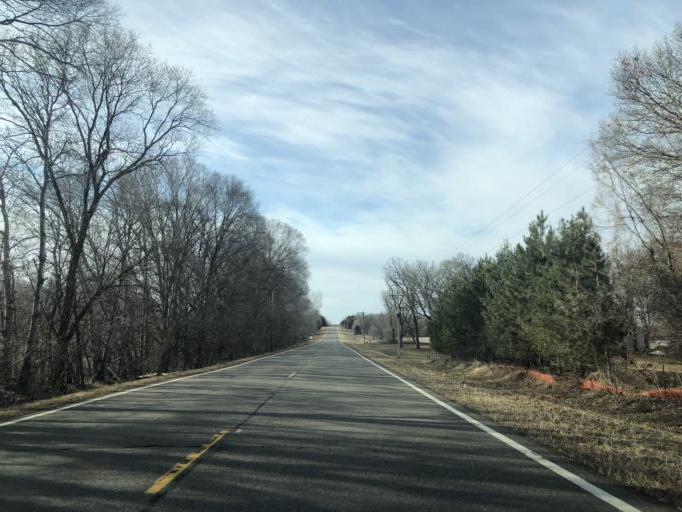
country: US
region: Minnesota
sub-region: Sherburne County
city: Becker
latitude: 45.4117
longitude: -93.8500
